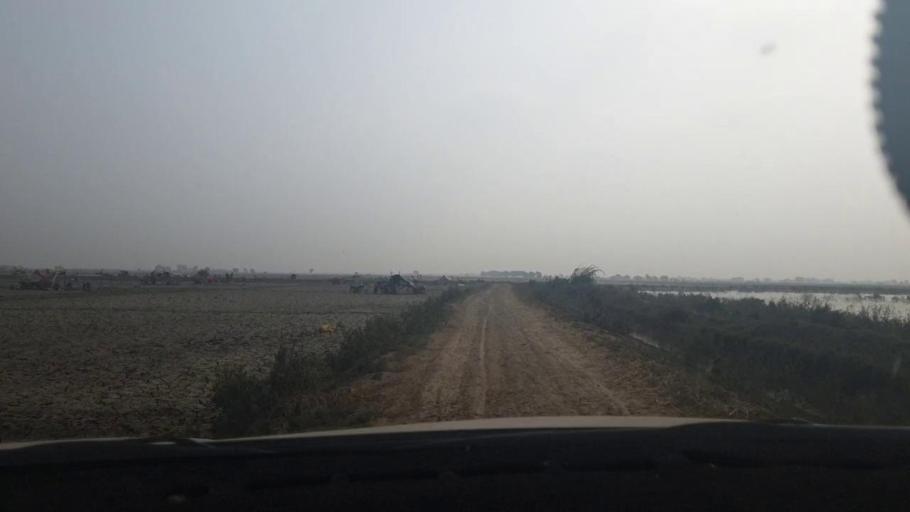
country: PK
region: Sindh
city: Tando Muhammad Khan
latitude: 25.0910
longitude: 68.5325
